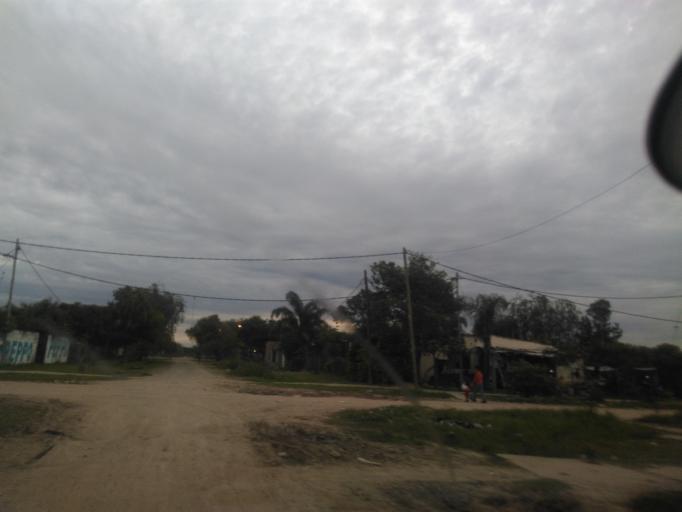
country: AR
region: Chaco
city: Resistencia
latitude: -27.4736
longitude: -59.0149
